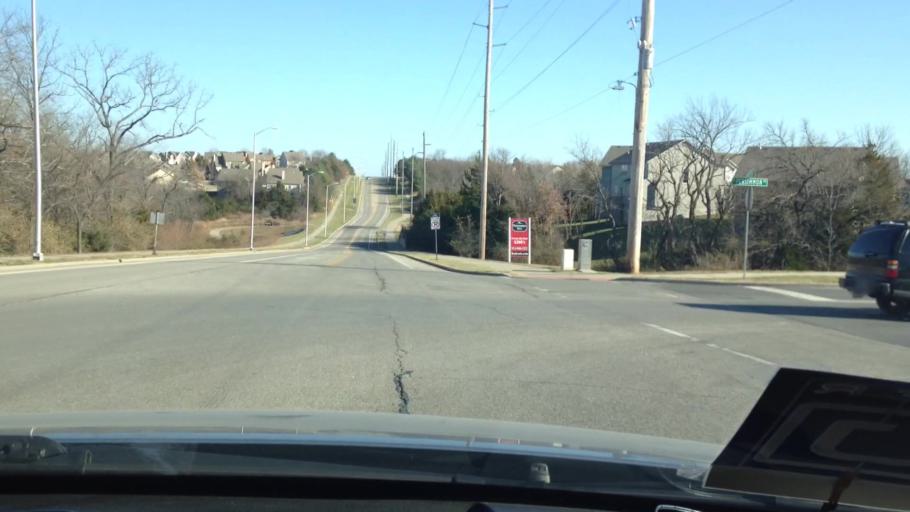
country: US
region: Kansas
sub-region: Johnson County
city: Olathe
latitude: 38.8982
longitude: -94.8663
